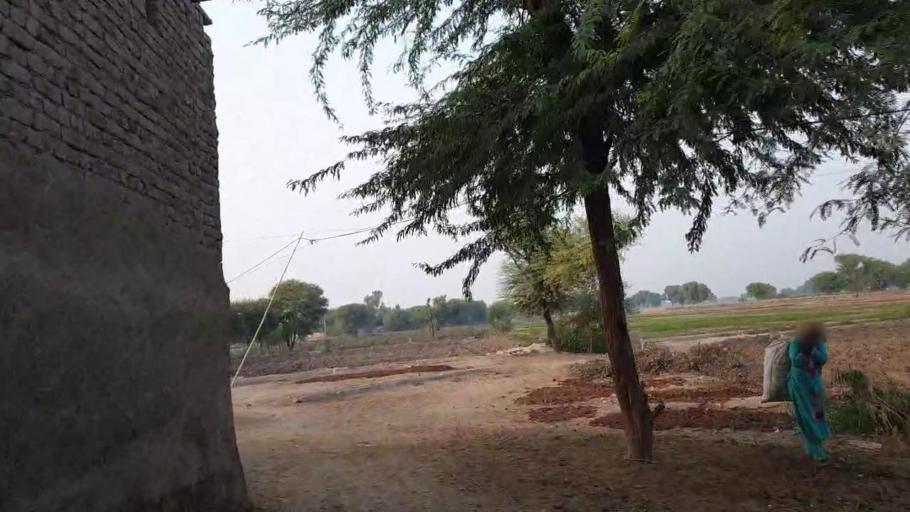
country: PK
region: Sindh
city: Bhan
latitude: 26.4972
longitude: 67.7283
